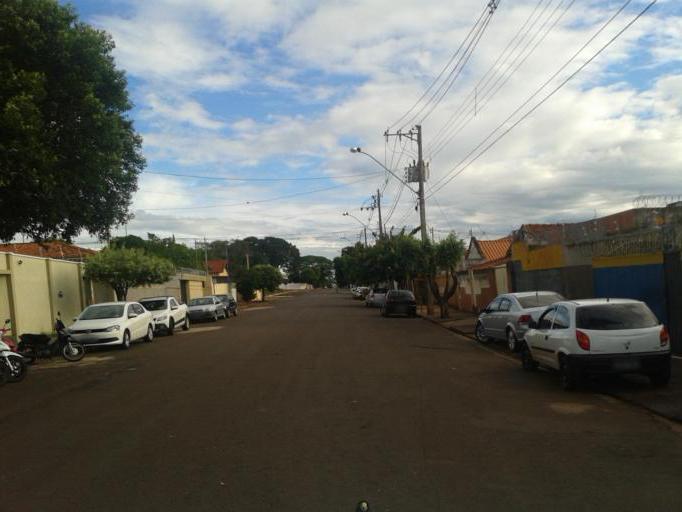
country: BR
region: Minas Gerais
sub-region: Ituiutaba
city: Ituiutaba
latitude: -18.9645
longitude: -49.4553
